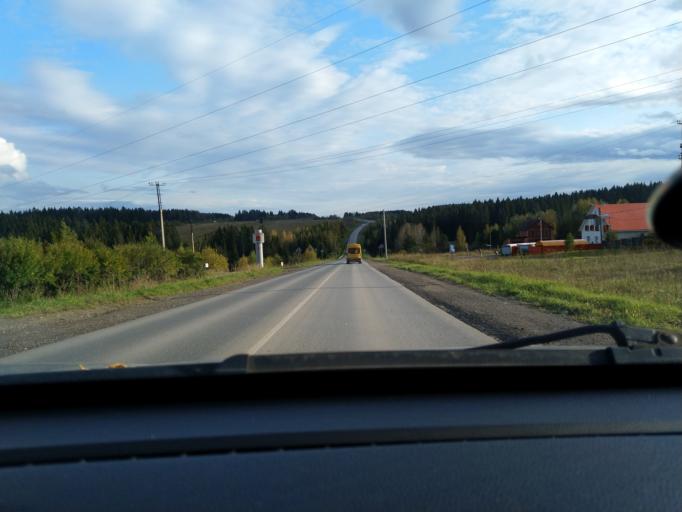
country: RU
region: Perm
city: Polazna
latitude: 58.2821
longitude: 56.4119
